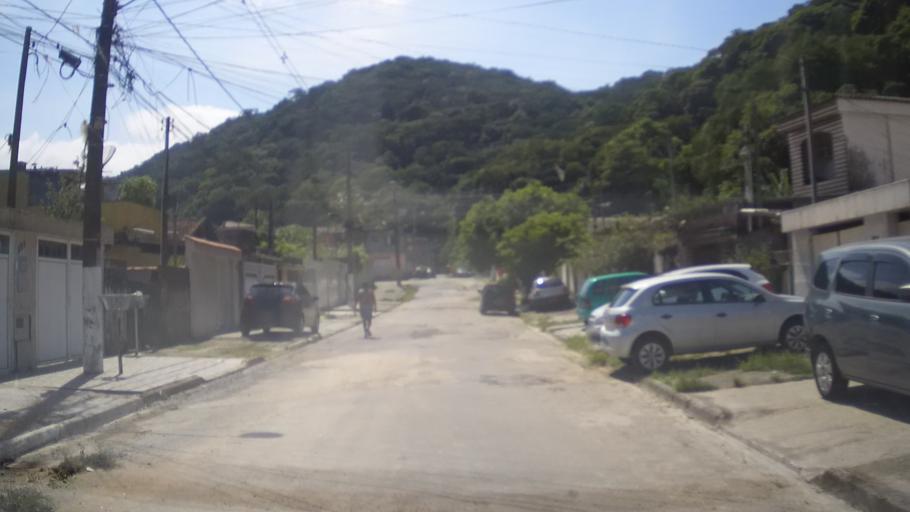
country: BR
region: Sao Paulo
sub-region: Praia Grande
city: Praia Grande
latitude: -23.9906
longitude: -46.3925
